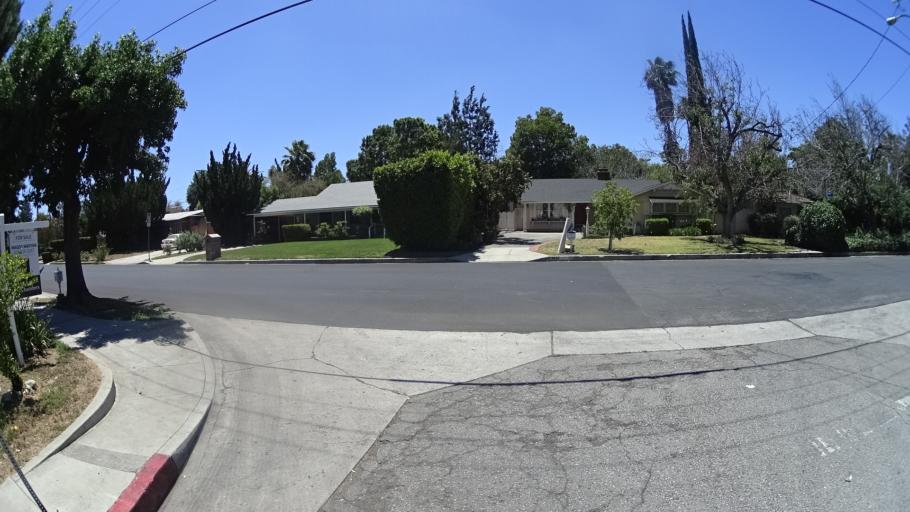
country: US
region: California
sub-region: Los Angeles County
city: Van Nuys
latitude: 34.1953
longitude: -118.4704
